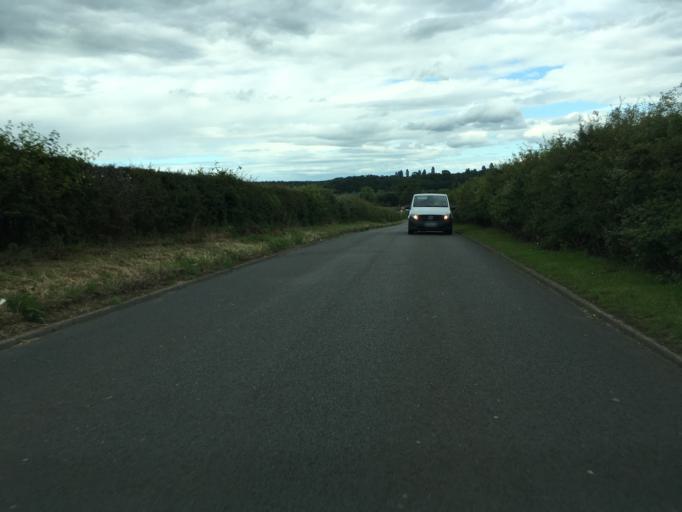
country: GB
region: England
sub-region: Central Bedfordshire
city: Leighton Buzzard
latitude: 51.9302
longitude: -0.6828
